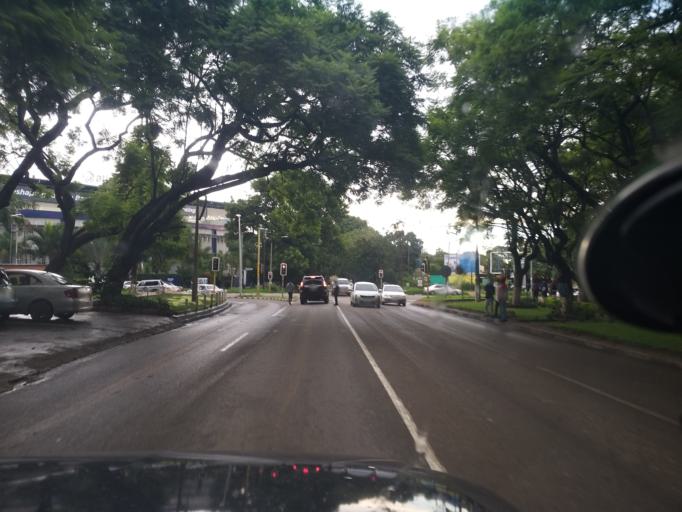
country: ZM
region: Lusaka
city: Lusaka
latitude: -15.4178
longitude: 28.3009
